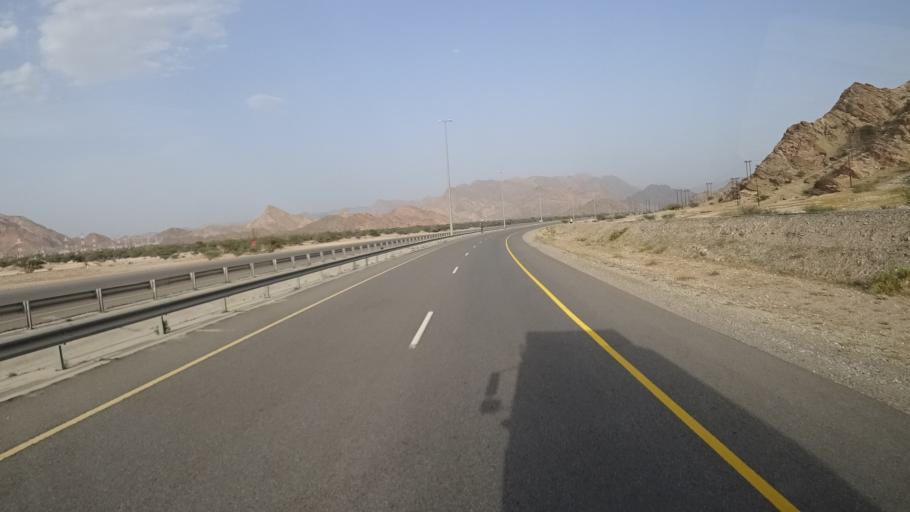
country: OM
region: Muhafazat Masqat
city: Muscat
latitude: 23.3683
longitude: 58.6415
